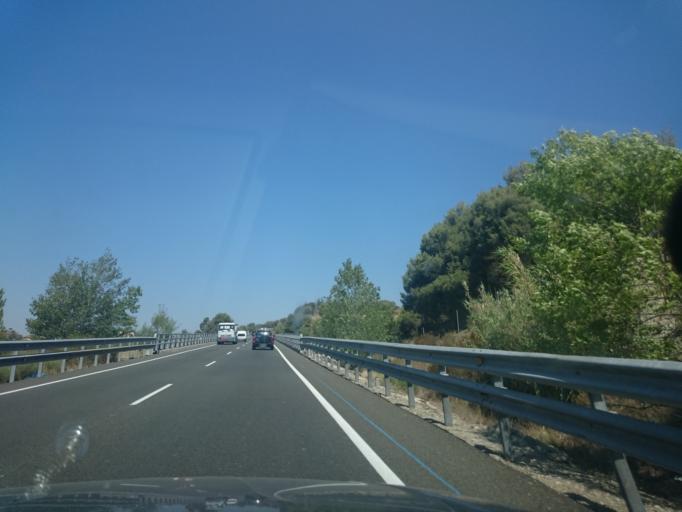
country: ES
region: Catalonia
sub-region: Provincia de Barcelona
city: La Pobla de Claramunt
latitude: 41.5551
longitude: 1.6863
